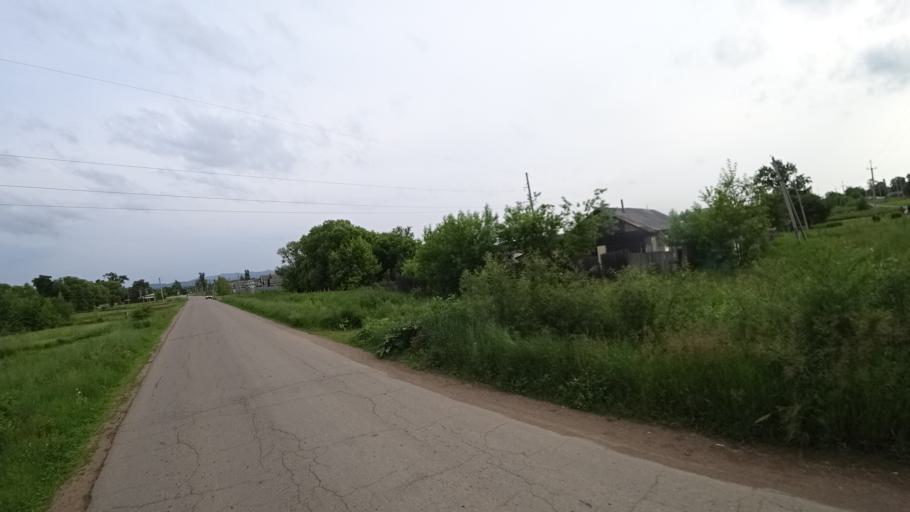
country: RU
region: Primorskiy
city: Novosysoyevka
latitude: 44.2340
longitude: 133.3706
